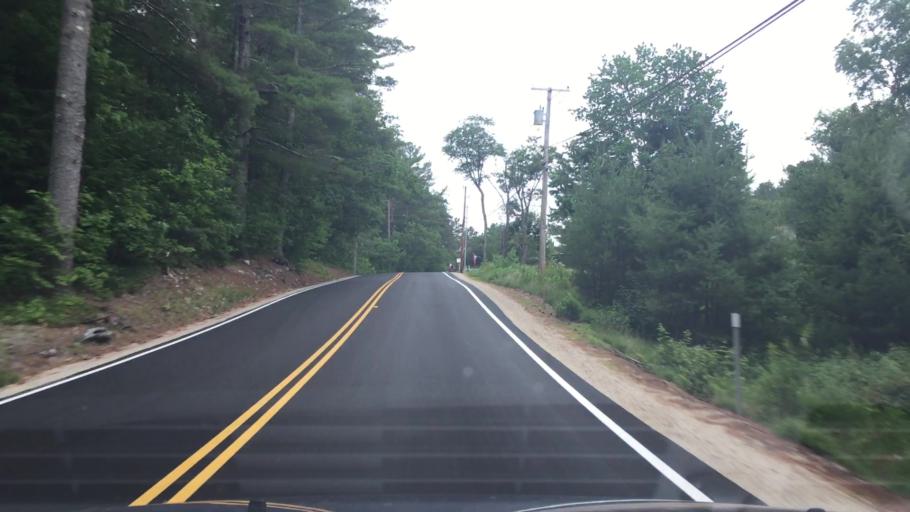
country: US
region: New Hampshire
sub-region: Carroll County
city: Madison
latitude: 43.8765
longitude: -71.0839
